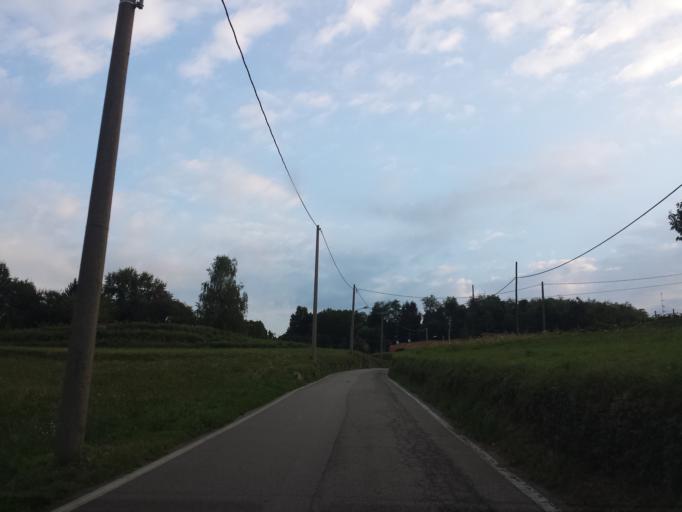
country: IT
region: Lombardy
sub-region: Provincia di Varese
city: Lisanza
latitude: 45.7373
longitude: 8.6125
